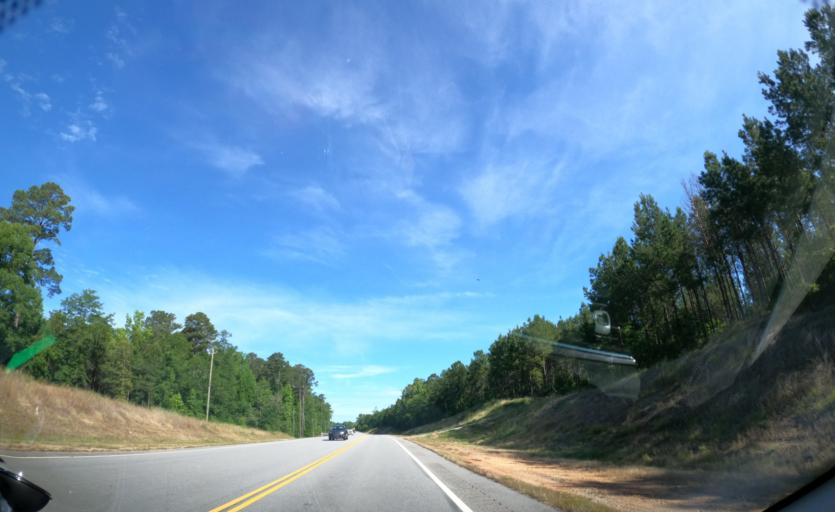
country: US
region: Georgia
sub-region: Columbia County
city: Appling
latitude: 33.6452
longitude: -82.3118
